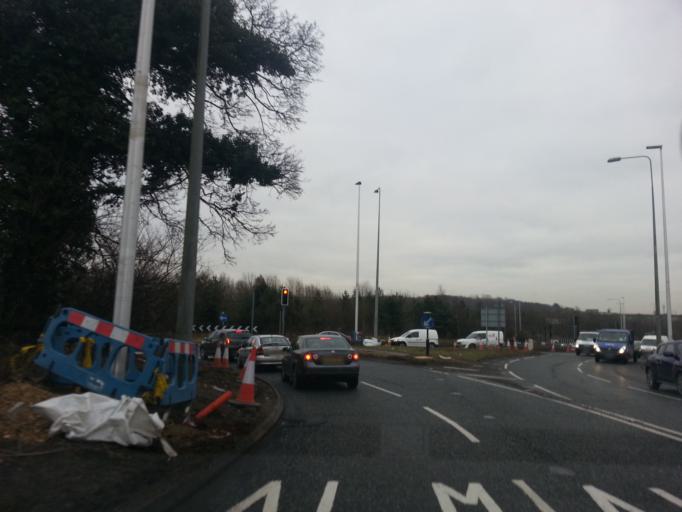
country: GB
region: England
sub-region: County Durham
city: Chester-le-Street
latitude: 54.8659
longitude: -1.5667
